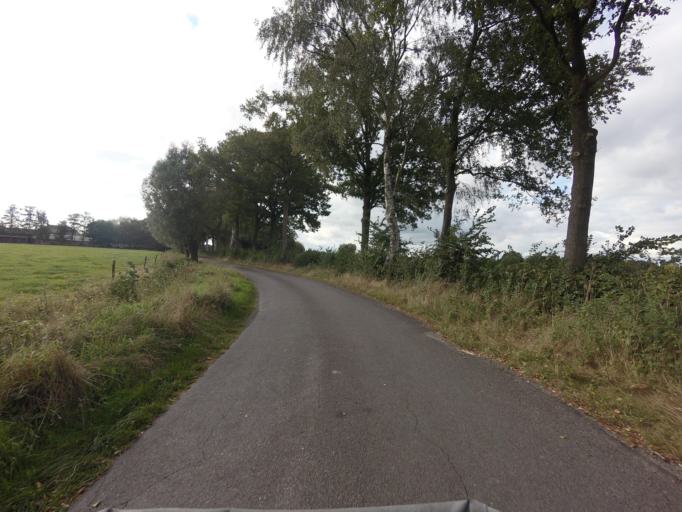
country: NL
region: Overijssel
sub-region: Gemeente Deventer
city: Schalkhaar
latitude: 52.2756
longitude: 6.2561
